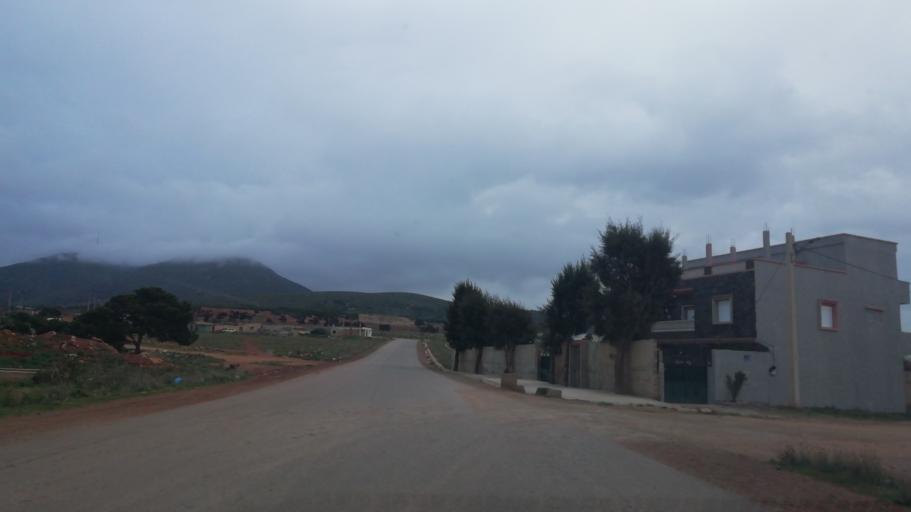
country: DZ
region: Oran
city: Bir el Djir
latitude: 35.7607
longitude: -0.5297
